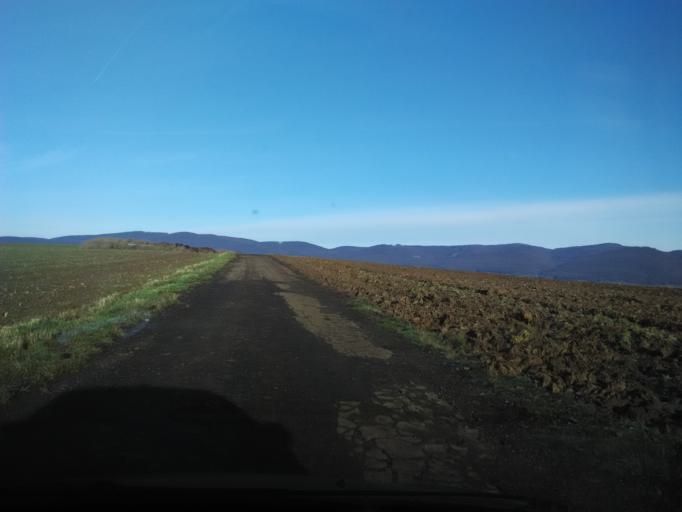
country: SK
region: Nitriansky
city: Tlmace
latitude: 48.3399
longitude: 18.5281
